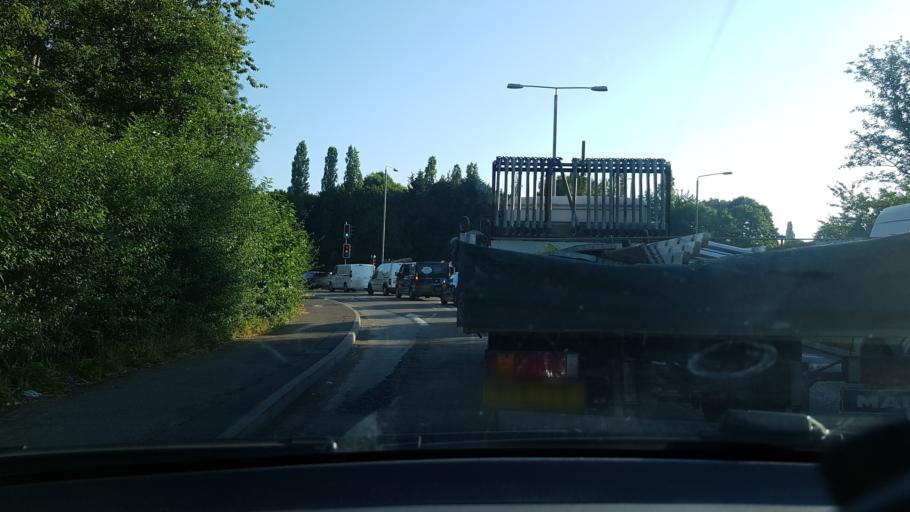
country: GB
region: England
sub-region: Nottinghamshire
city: Awsworth
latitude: 52.9987
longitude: -1.2800
